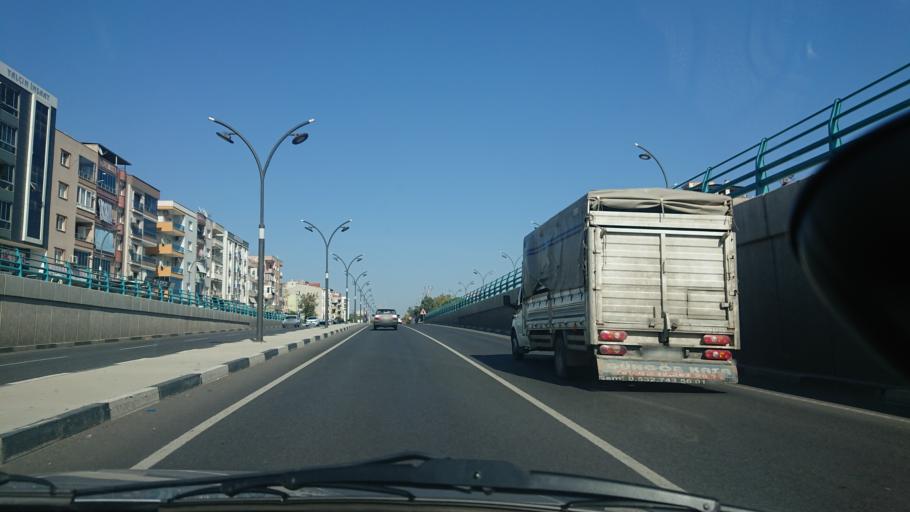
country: TR
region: Manisa
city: Turgutlu
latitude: 38.4919
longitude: 27.7099
